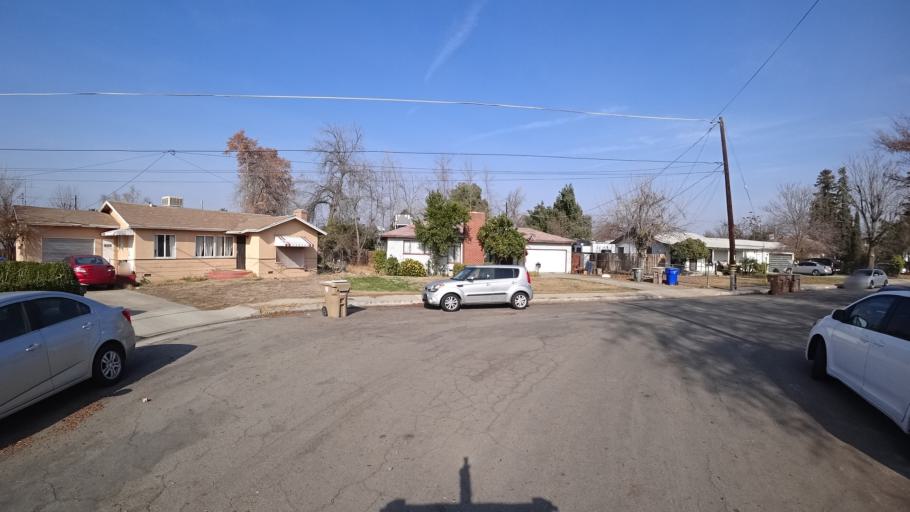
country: US
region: California
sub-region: Kern County
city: Bakersfield
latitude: 35.3640
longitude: -119.0338
